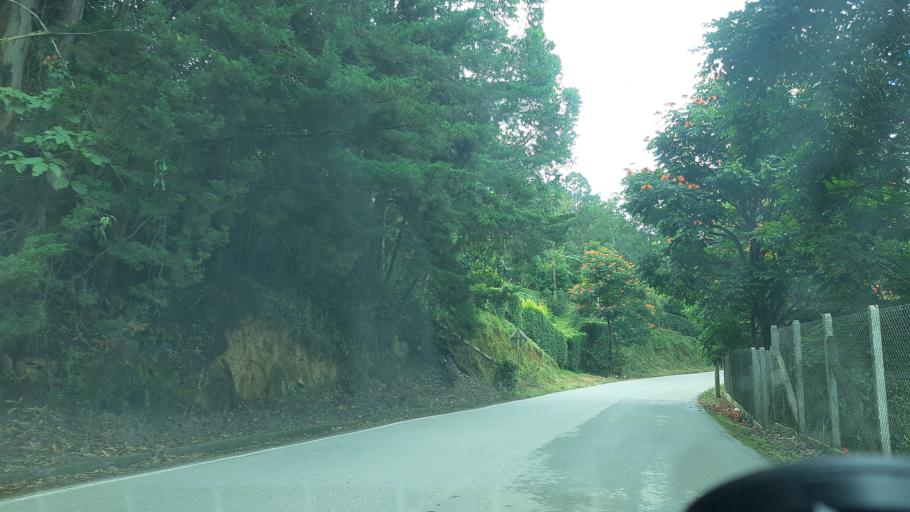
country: CO
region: Boyaca
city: Garagoa
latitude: 5.0596
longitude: -73.3828
